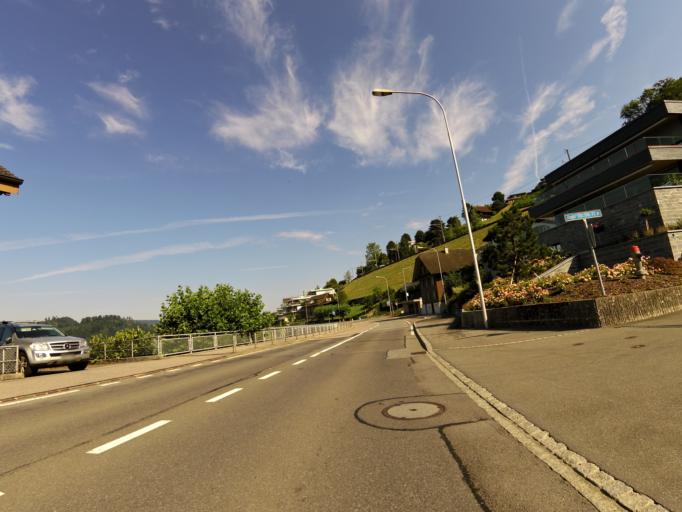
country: CH
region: Zug
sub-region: Zug
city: Walchwil
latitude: 47.1070
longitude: 8.5061
